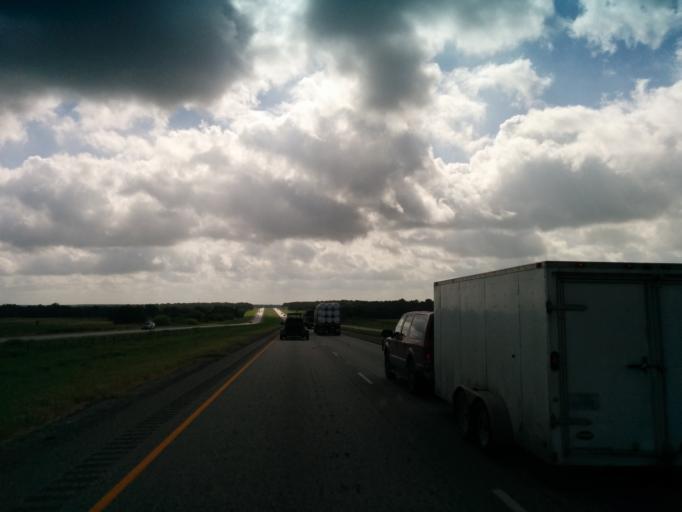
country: US
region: Texas
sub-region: Gonzales County
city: Waelder
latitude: 29.6586
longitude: -97.4121
